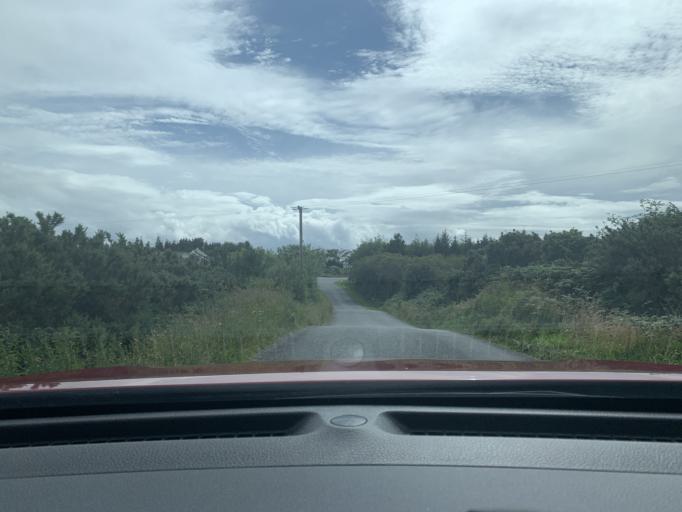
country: IE
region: Ulster
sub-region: County Donegal
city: Dungloe
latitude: 54.9418
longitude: -8.3587
